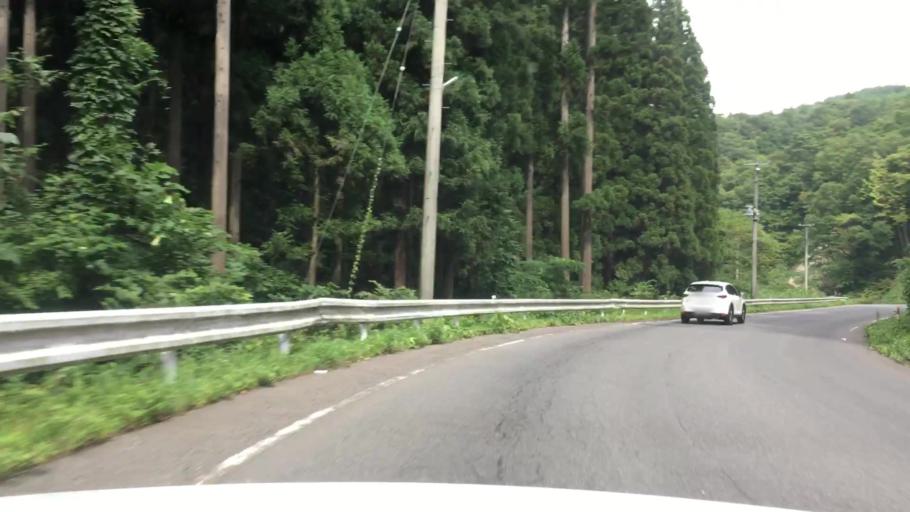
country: JP
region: Aomori
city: Shimokizukuri
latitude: 40.7342
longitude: 140.2497
